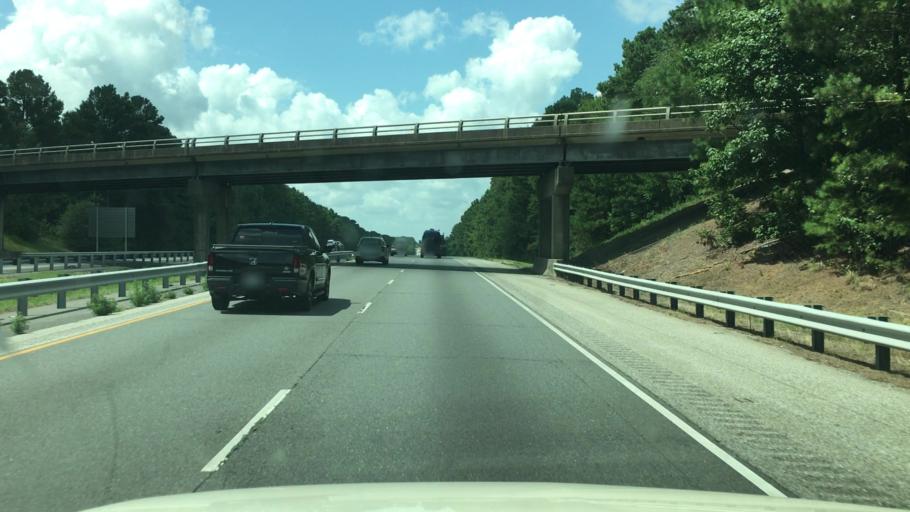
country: US
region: Arkansas
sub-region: Clark County
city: Arkadelphia
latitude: 34.0931
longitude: -93.1080
